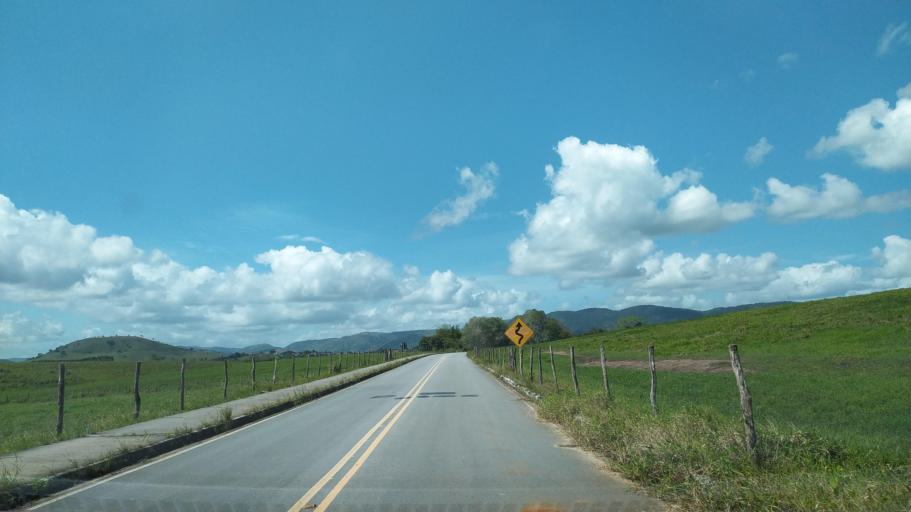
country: BR
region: Alagoas
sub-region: Uniao Dos Palmares
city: Uniao dos Palmares
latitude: -9.1629
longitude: -36.0516
